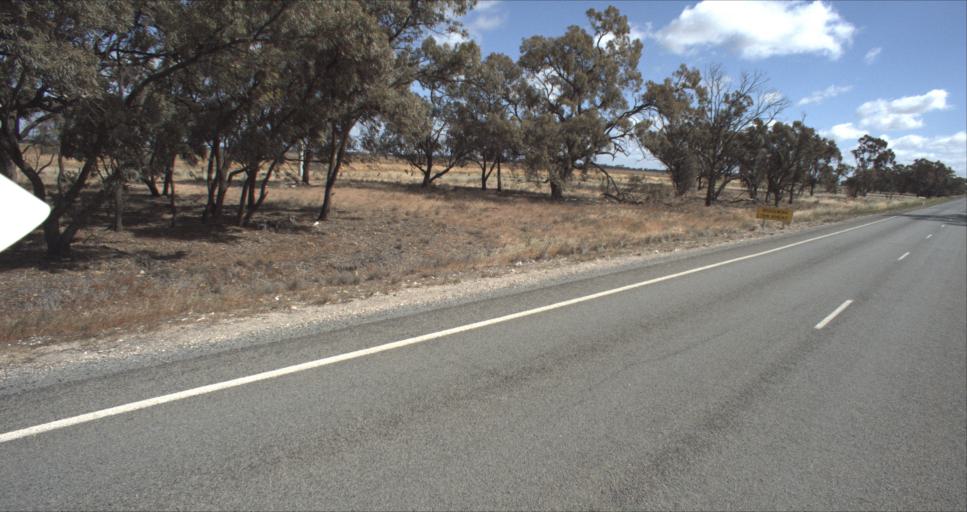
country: AU
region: New South Wales
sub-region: Murrumbidgee Shire
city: Darlington Point
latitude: -34.5627
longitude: 146.1687
